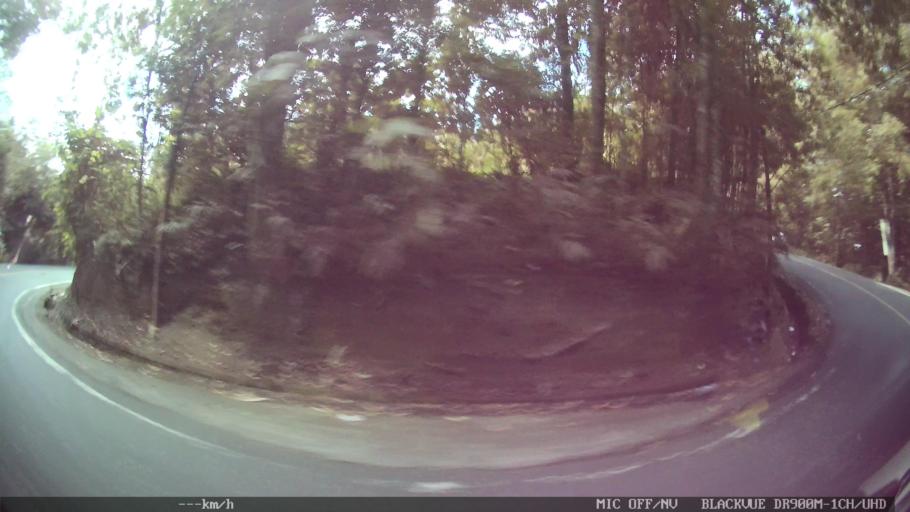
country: ID
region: Bali
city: Banjar Kedisan
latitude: -8.2855
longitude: 115.3658
